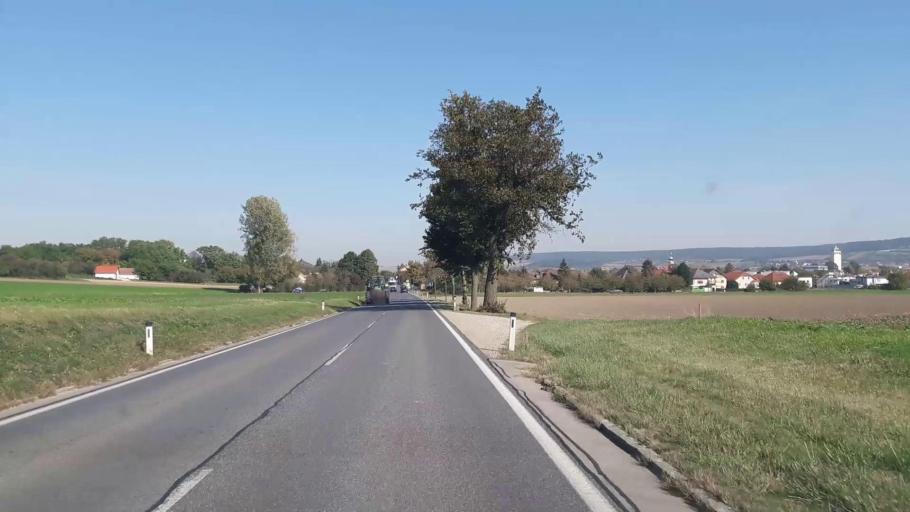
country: AT
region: Lower Austria
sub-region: Politischer Bezirk Korneuburg
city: Harmannsdorf
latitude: 48.3868
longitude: 16.3621
